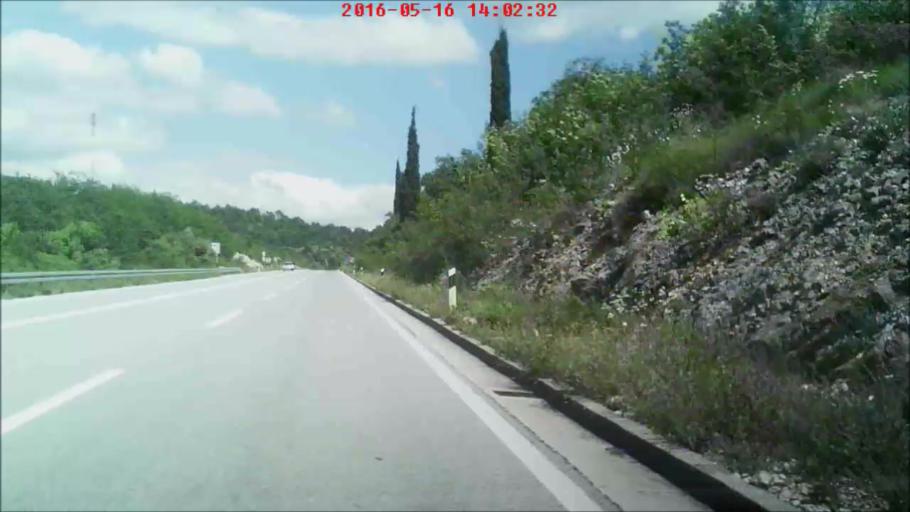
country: HR
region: Dubrovacko-Neretvanska
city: Ston
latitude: 42.8241
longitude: 17.7593
